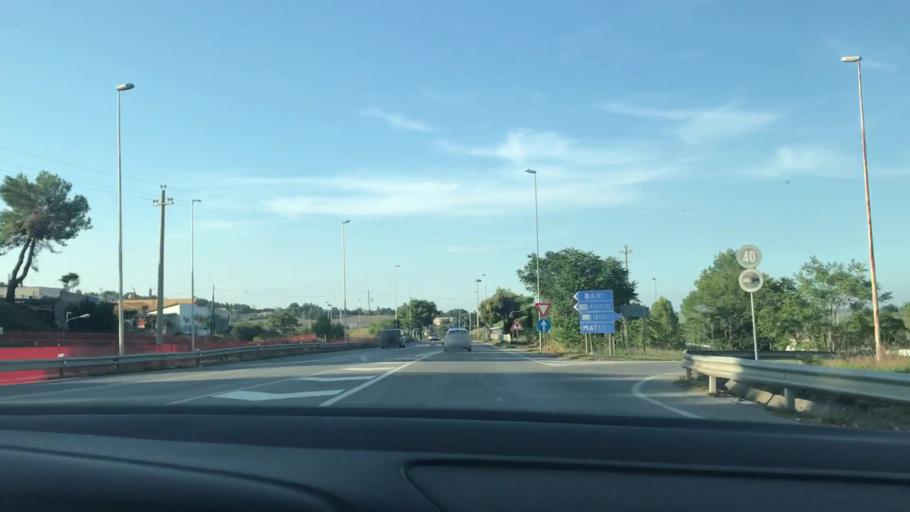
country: IT
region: Basilicate
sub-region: Provincia di Matera
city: Matera
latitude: 40.6835
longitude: 16.5902
